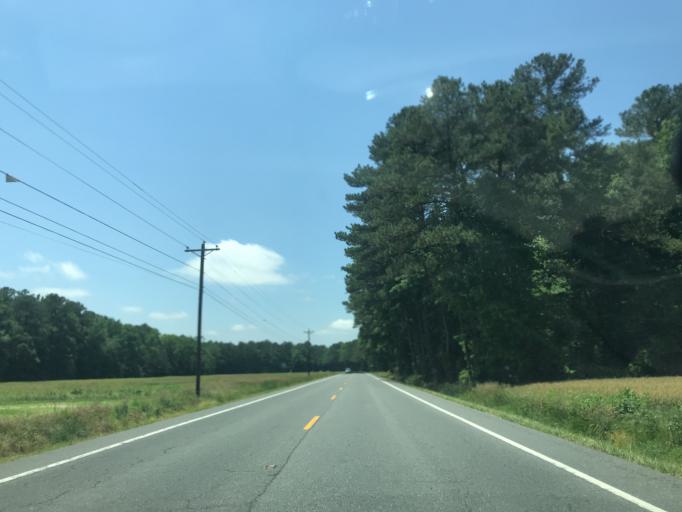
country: US
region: Maryland
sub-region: Caroline County
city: Federalsburg
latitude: 38.6332
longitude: -75.7800
